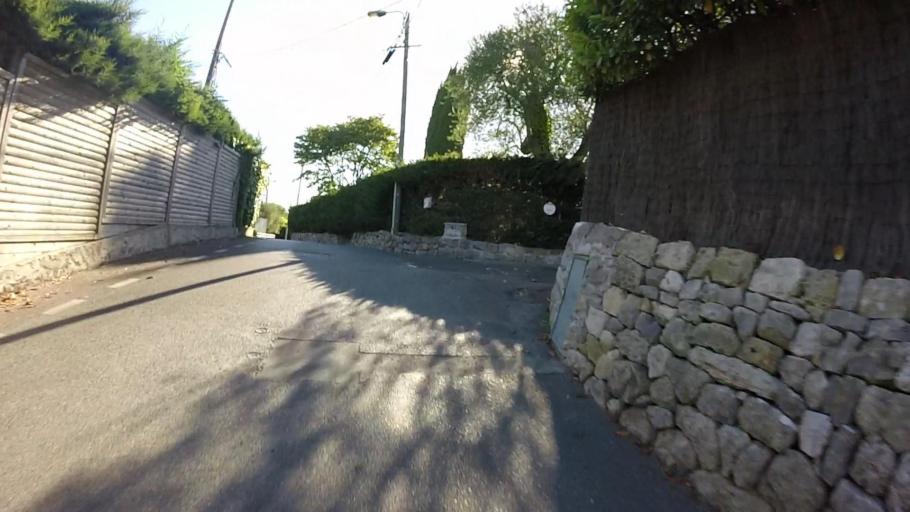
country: FR
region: Provence-Alpes-Cote d'Azur
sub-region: Departement des Alpes-Maritimes
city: Mougins
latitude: 43.6070
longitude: 7.0020
